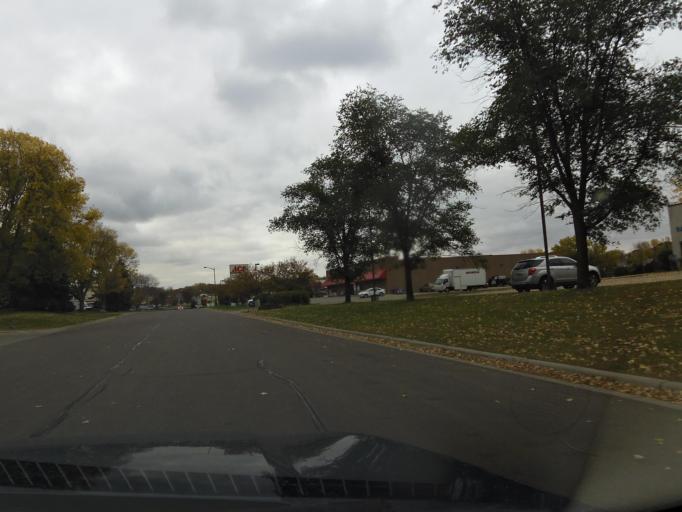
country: US
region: Minnesota
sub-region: Dakota County
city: Lakeville
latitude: 44.6919
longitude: -93.2867
